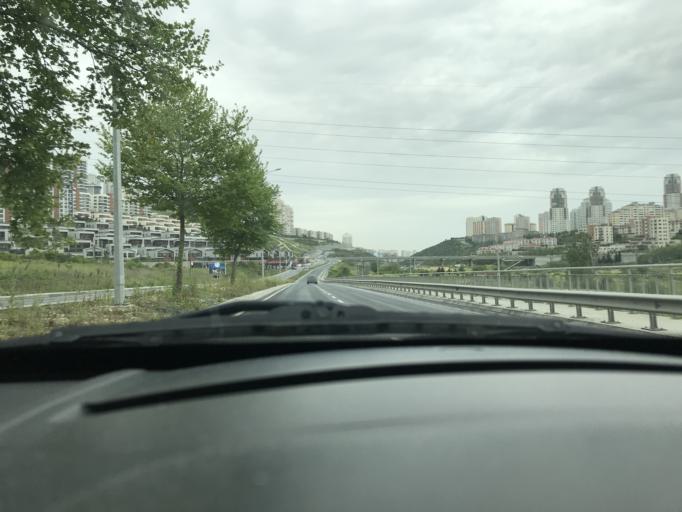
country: TR
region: Istanbul
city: Esenyurt
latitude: 41.0843
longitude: 28.6799
